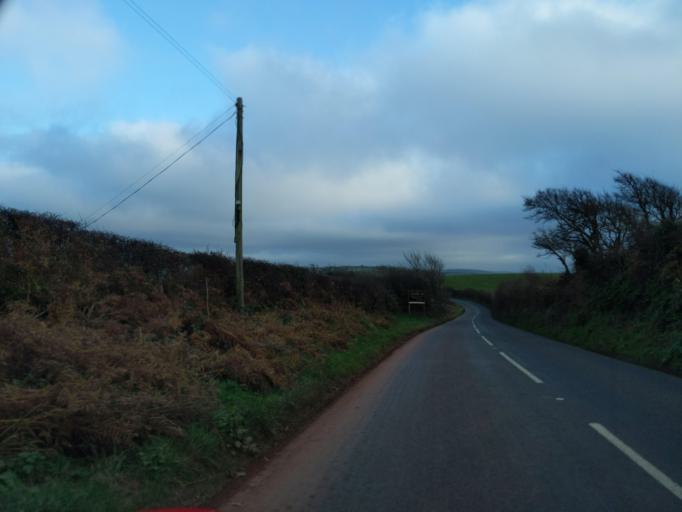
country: GB
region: England
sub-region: Cornwall
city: Saltash
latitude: 50.3637
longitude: -4.2949
